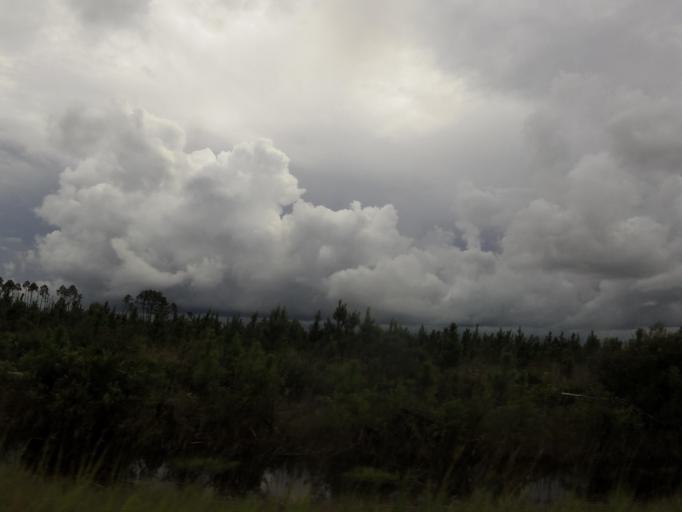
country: US
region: Florida
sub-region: Baker County
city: Macclenny
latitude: 30.5176
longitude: -82.1162
